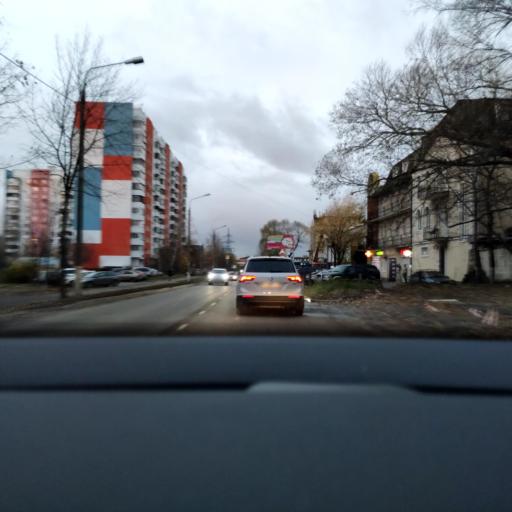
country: RU
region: Moskovskaya
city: Reutov
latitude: 55.7695
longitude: 37.8651
